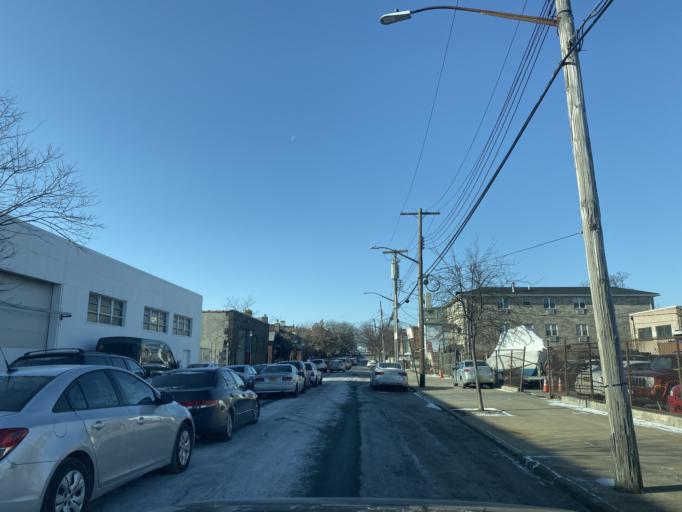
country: US
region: New York
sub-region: Bronx
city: The Bronx
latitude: 40.8320
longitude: -73.8450
